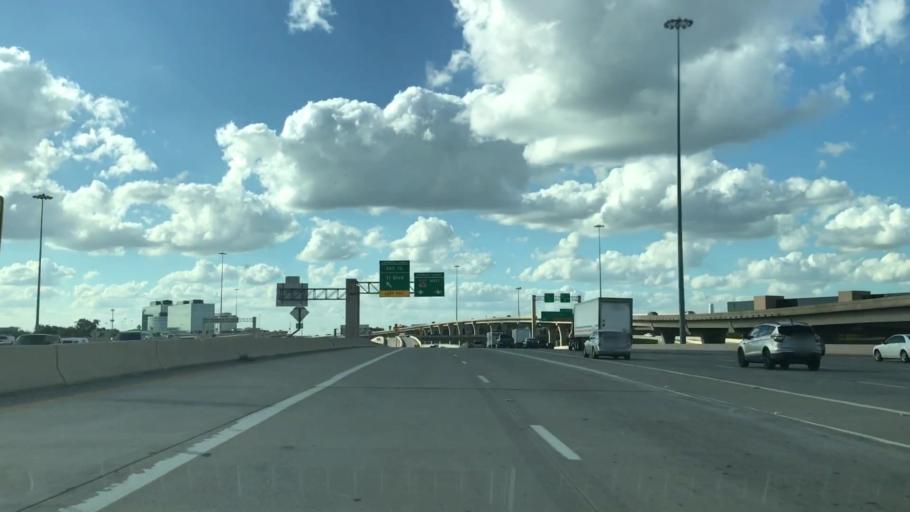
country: US
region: Texas
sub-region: Dallas County
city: Richardson
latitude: 32.9206
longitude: -96.7495
